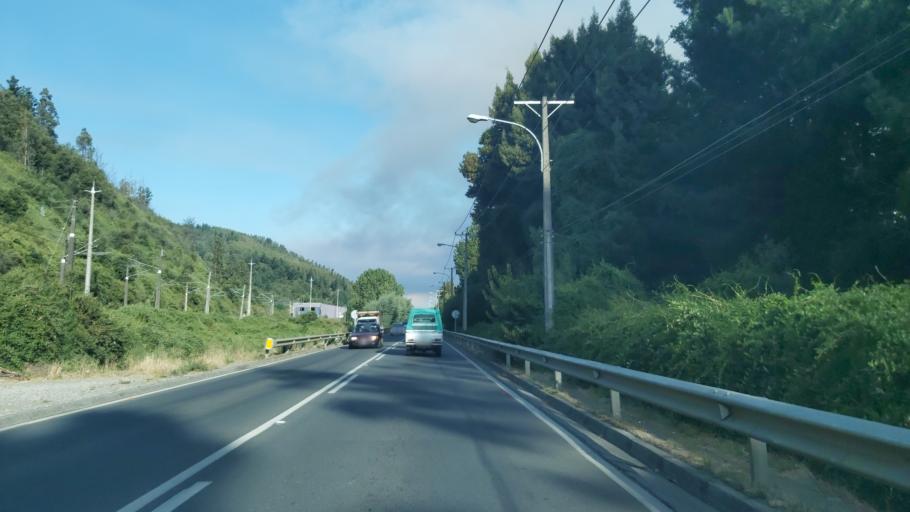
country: CL
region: Biobio
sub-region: Provincia de Concepcion
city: Chiguayante
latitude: -36.9653
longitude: -73.0042
